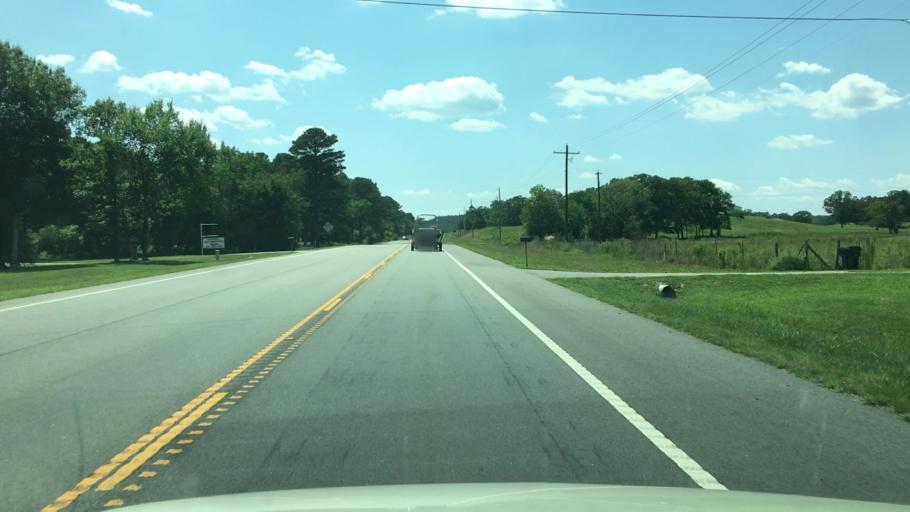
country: US
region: Arkansas
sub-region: Garland County
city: Piney
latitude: 34.5108
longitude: -93.2230
